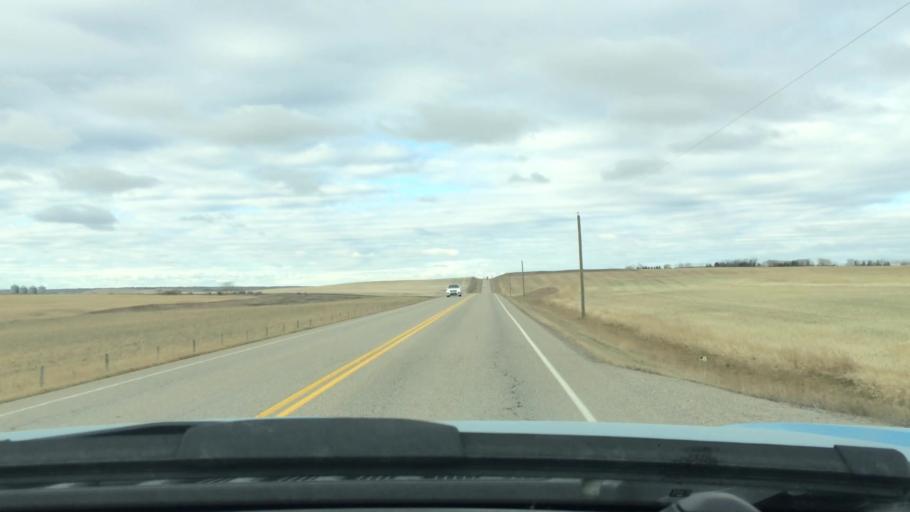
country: CA
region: Alberta
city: Airdrie
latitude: 51.2125
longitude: -114.1083
